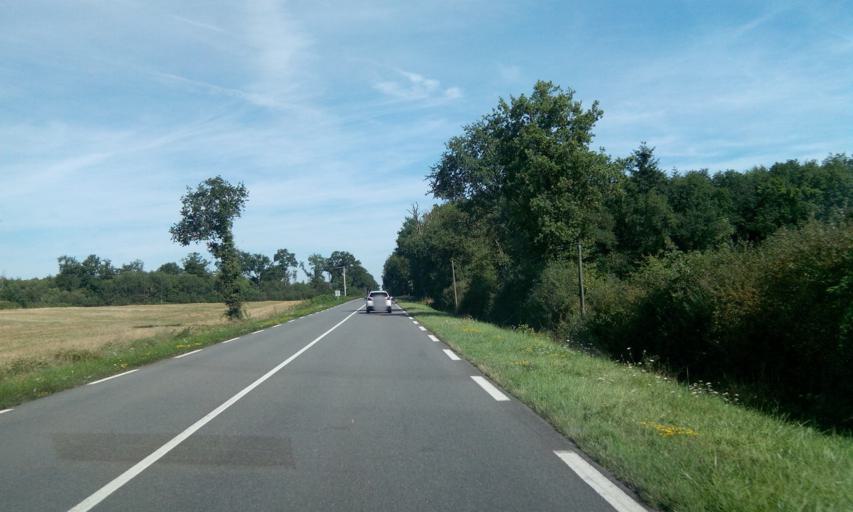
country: FR
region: Poitou-Charentes
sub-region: Departement de la Vienne
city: Availles-Limouzine
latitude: 46.0734
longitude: 0.5925
